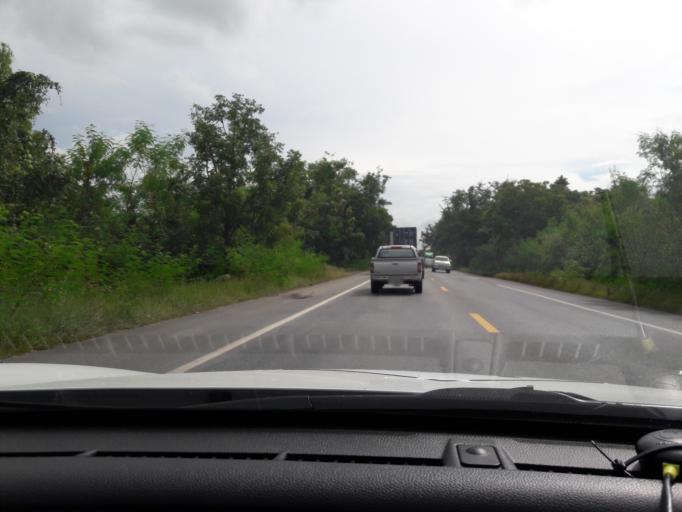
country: TH
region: Nakhon Sawan
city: Phai Sali
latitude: 15.5509
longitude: 100.5551
